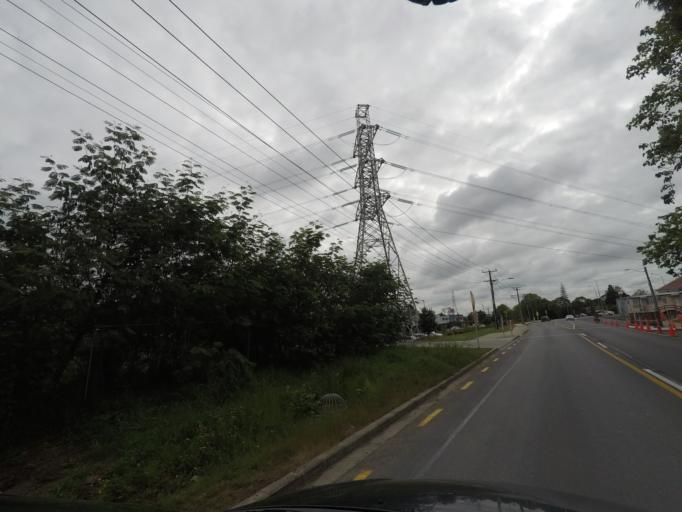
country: NZ
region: Auckland
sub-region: Auckland
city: Rosebank
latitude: -36.8371
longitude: 174.5997
